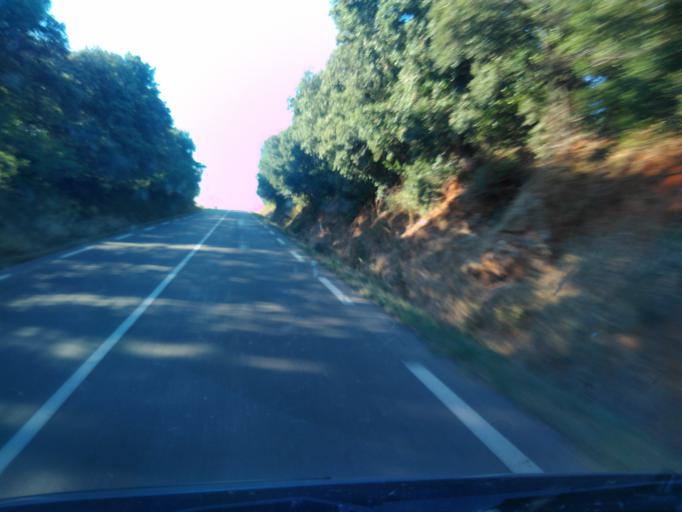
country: FR
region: Languedoc-Roussillon
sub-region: Departement du Gard
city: Vauvert
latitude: 43.6705
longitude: 4.2823
